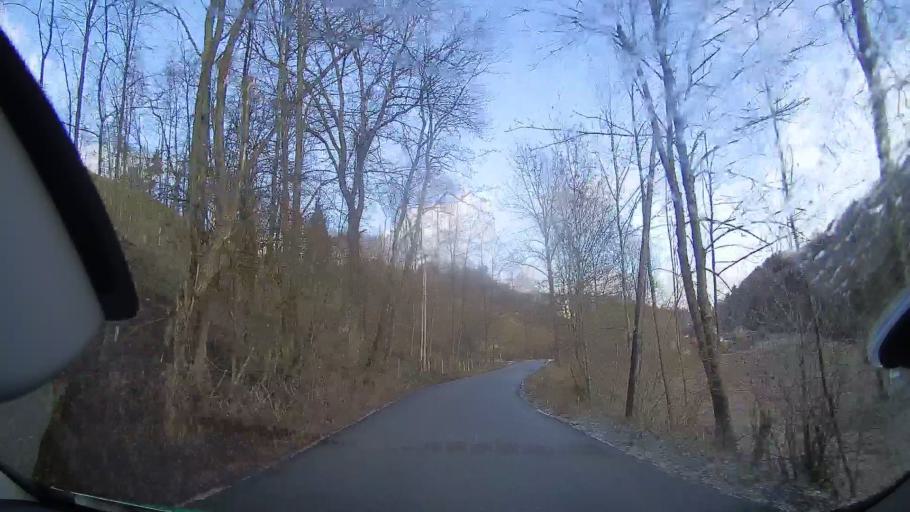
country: RO
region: Alba
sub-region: Comuna Sohodol
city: Sohodol
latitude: 46.3418
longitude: 23.0147
